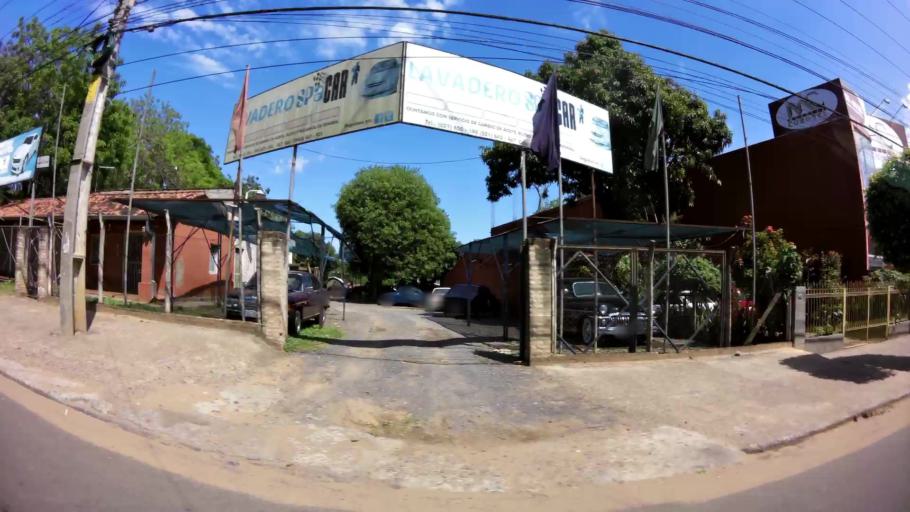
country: PY
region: Central
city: San Lorenzo
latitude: -25.2806
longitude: -57.4983
